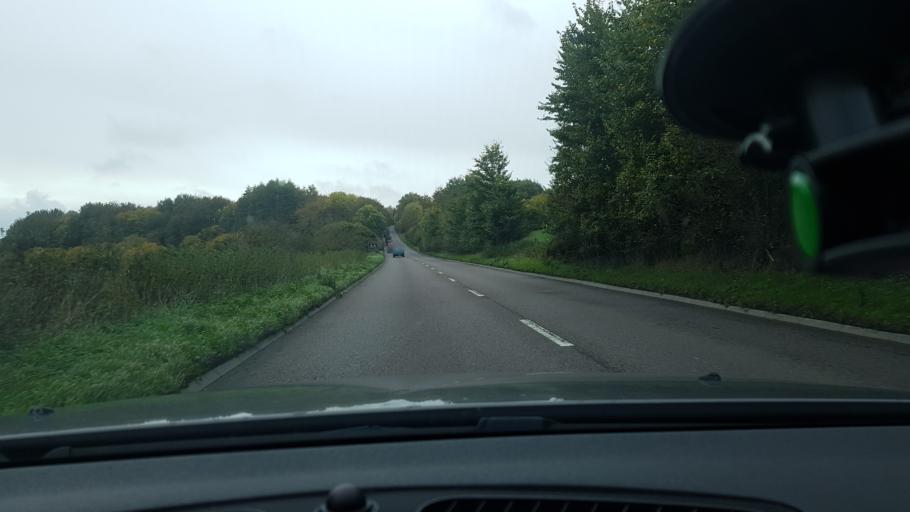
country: GB
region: England
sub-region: Wiltshire
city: Marlborough
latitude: 51.4336
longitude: -1.7310
